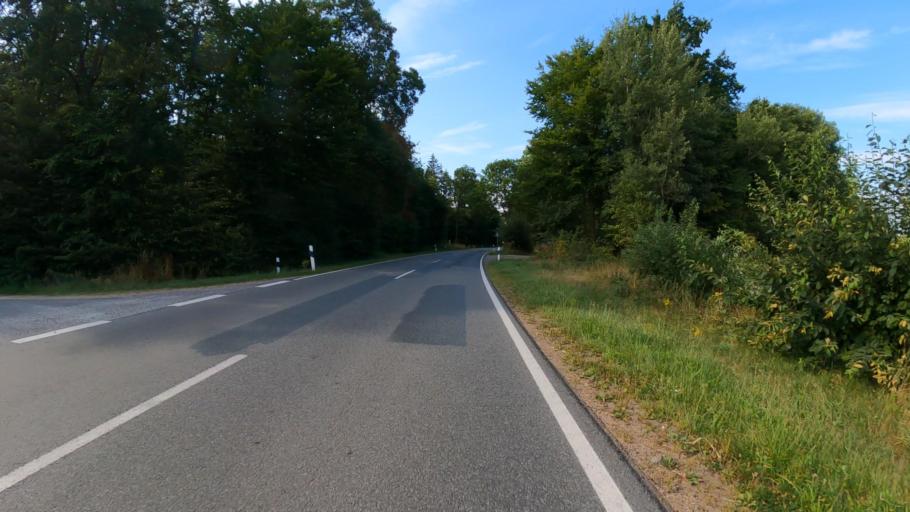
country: DE
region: Schleswig-Holstein
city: Brunstorf
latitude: 53.4836
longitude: 10.4255
